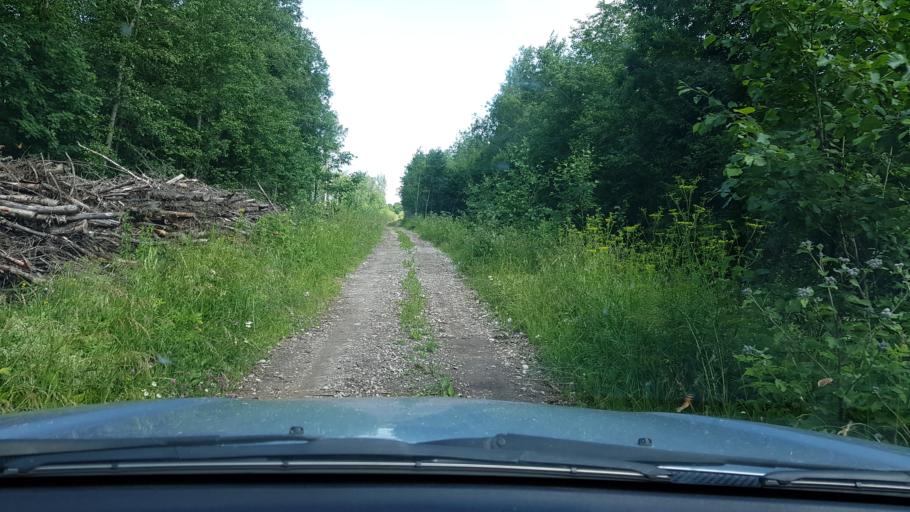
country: EE
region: Ida-Virumaa
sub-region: Sillamaee linn
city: Sillamae
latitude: 59.3579
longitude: 27.7813
